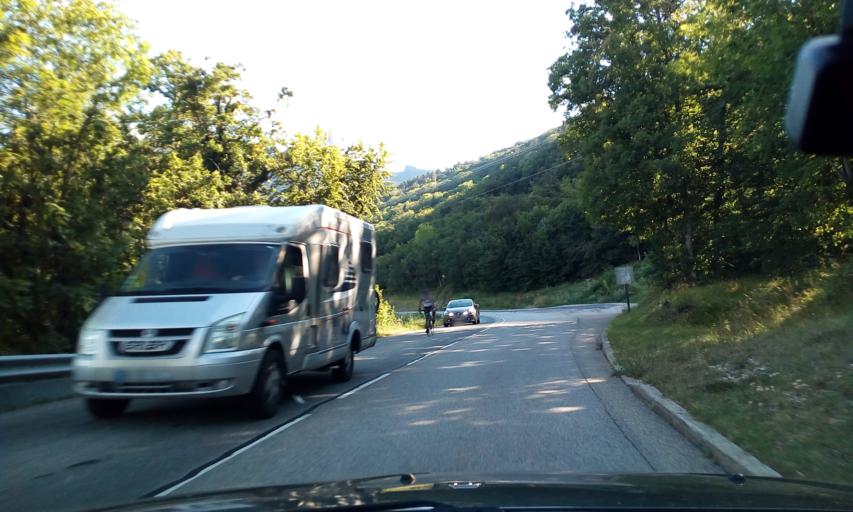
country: FR
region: Rhone-Alpes
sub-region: Departement de l'Isere
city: Sassenage
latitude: 45.1778
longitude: 5.6521
